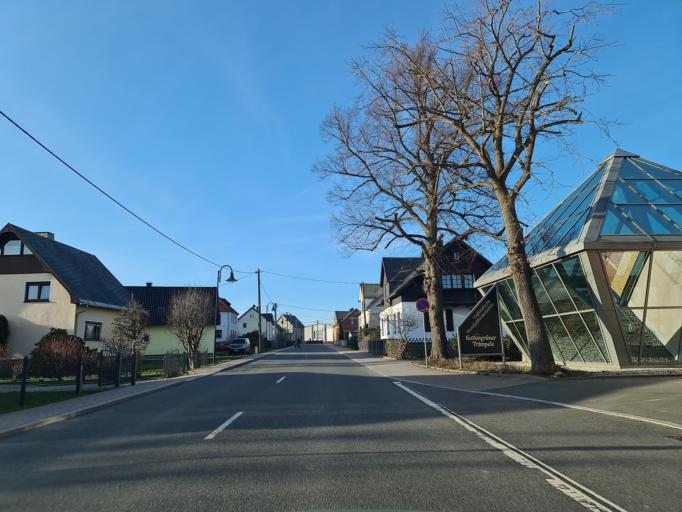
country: DE
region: Saxony
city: Grunbach
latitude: 50.4412
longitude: 12.3642
